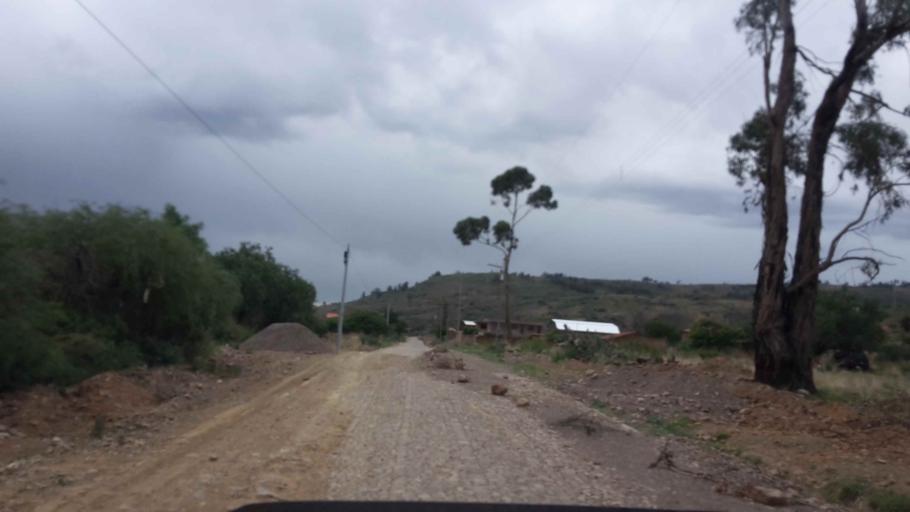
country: BO
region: Cochabamba
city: Cochabamba
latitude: -17.5393
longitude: -66.1997
